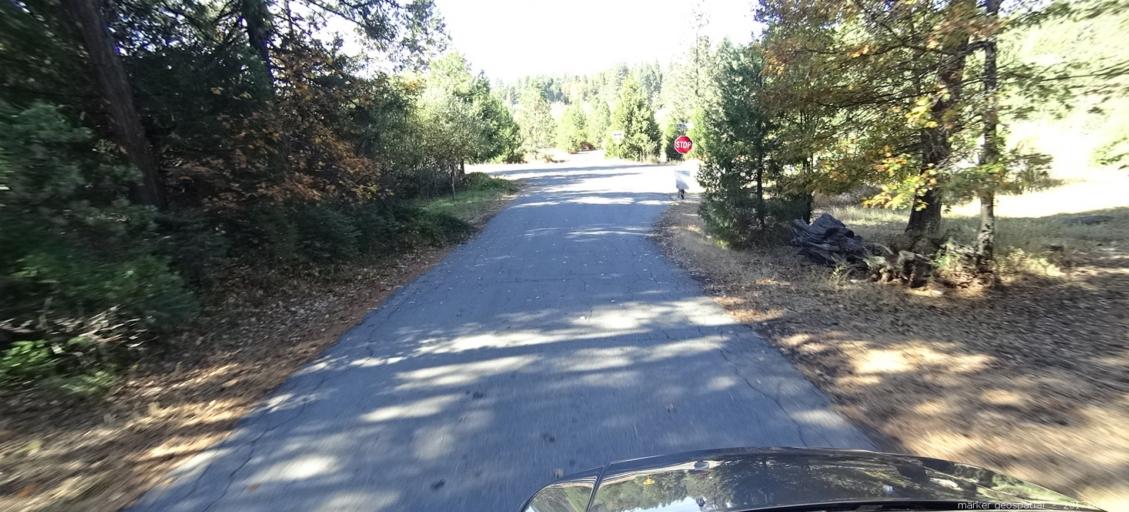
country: US
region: California
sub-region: Shasta County
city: Shingletown
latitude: 40.4921
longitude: -121.8824
